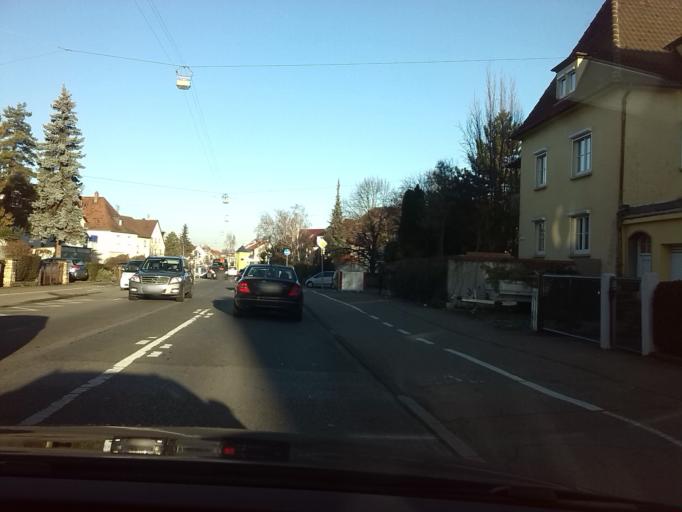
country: DE
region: Baden-Wuerttemberg
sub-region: Regierungsbezirk Stuttgart
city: Fellbach
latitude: 48.8262
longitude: 9.2684
